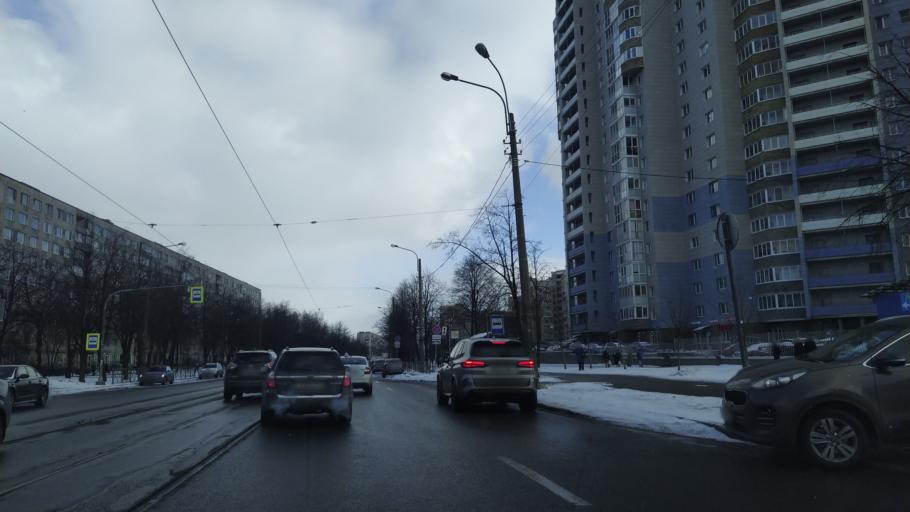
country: RU
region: Leningrad
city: Akademicheskoe
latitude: 60.0148
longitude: 30.3901
